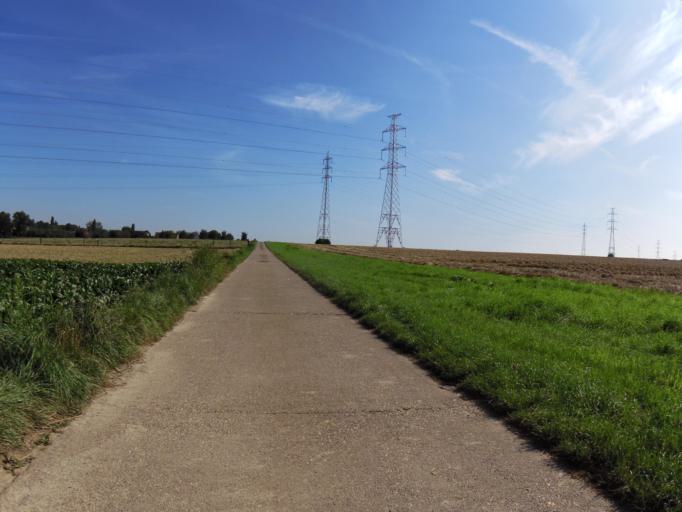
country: BE
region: Flanders
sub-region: Provincie Limburg
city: Riemst
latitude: 50.7984
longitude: 5.5725
